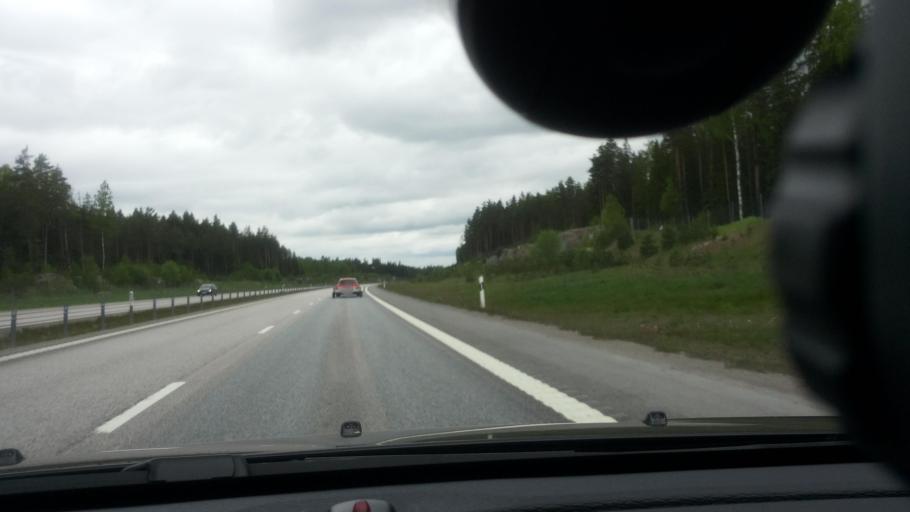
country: SE
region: Uppsala
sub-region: Osthammars Kommun
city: Bjorklinge
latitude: 60.1819
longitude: 17.5042
